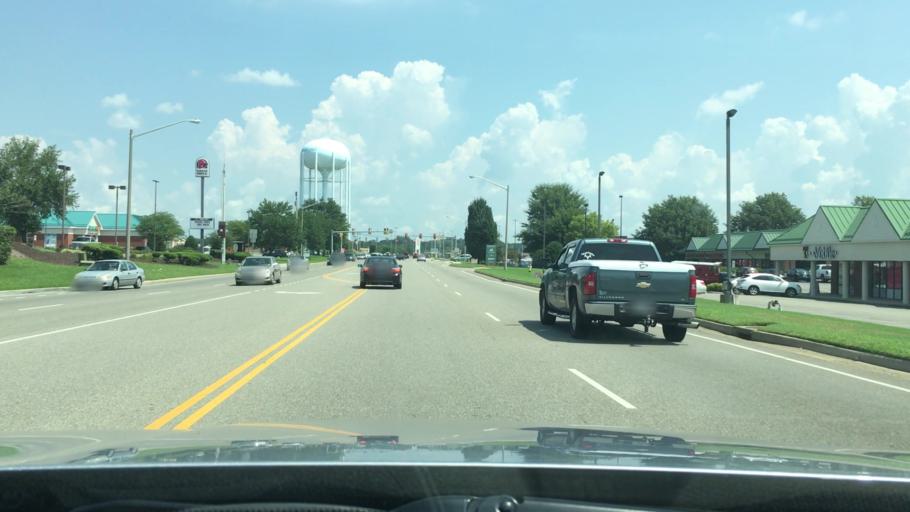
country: US
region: Virginia
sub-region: City of Petersburg
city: Petersburg
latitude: 37.2445
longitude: -77.3905
